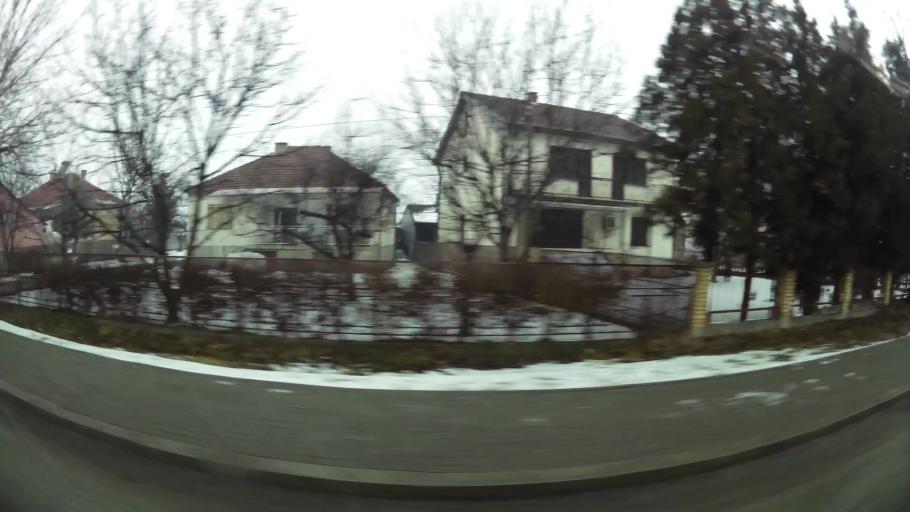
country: MK
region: Petrovec
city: Petrovec
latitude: 41.9334
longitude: 21.6223
